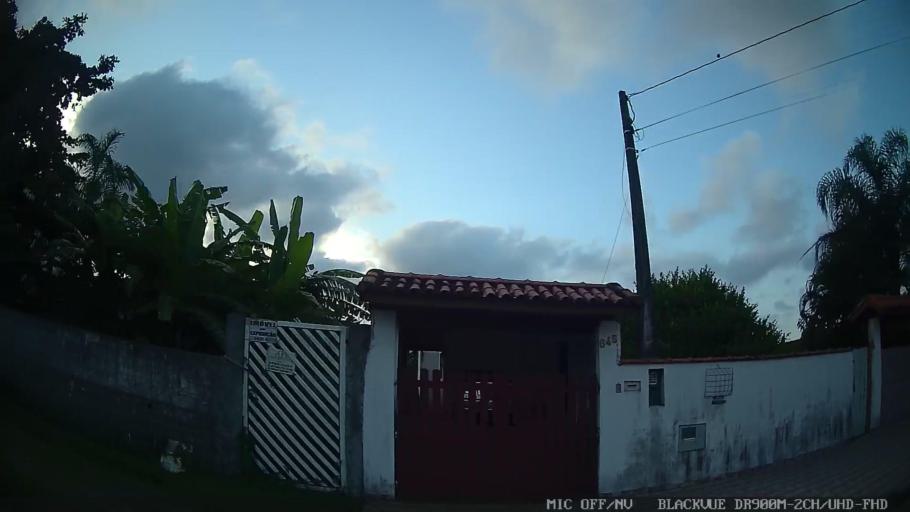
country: BR
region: Sao Paulo
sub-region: Peruibe
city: Peruibe
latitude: -24.3162
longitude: -46.9985
